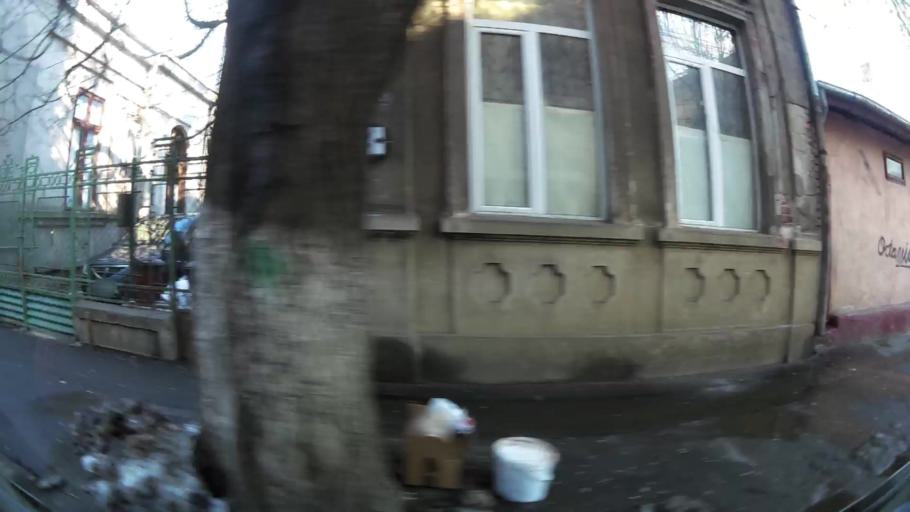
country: RO
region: Bucuresti
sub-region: Municipiul Bucuresti
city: Bucharest
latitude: 44.4370
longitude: 26.1213
